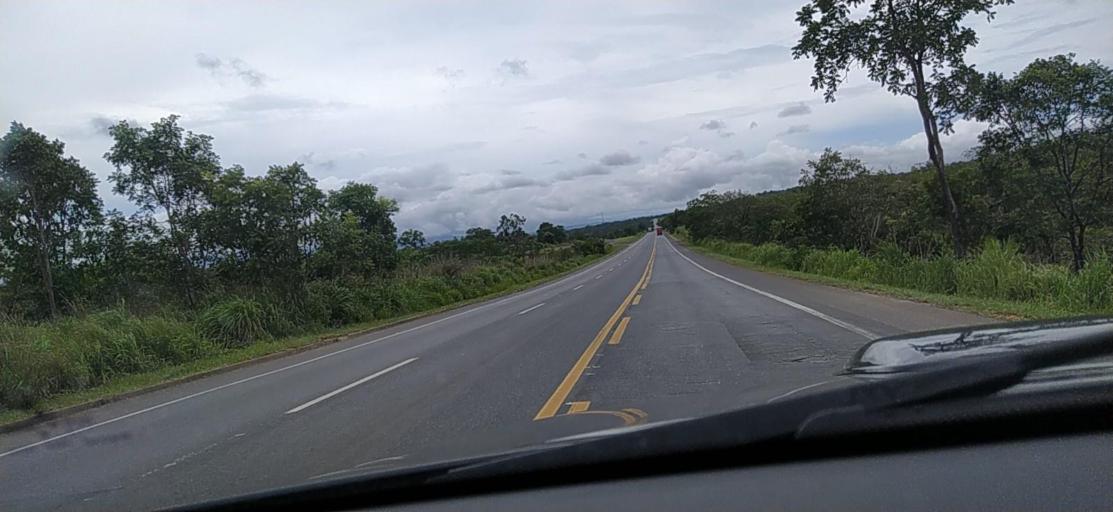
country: BR
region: Minas Gerais
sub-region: Corinto
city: Corinto
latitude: -18.3182
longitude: -44.4240
